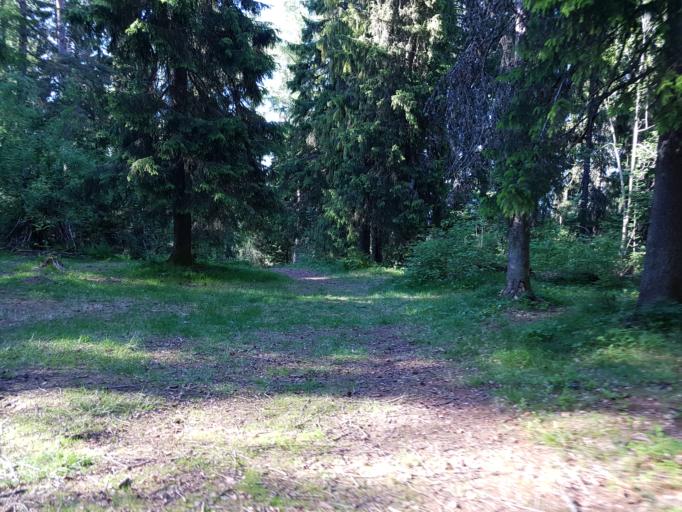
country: NO
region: Sor-Trondelag
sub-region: Trondheim
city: Trondheim
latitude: 63.4221
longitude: 10.3627
